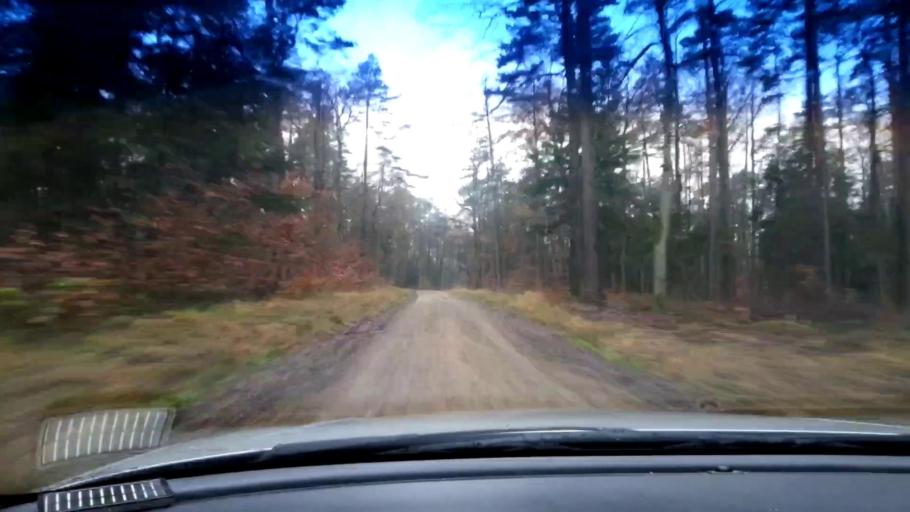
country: DE
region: Bavaria
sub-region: Upper Franconia
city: Gundelsheim
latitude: 49.9531
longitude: 10.9166
